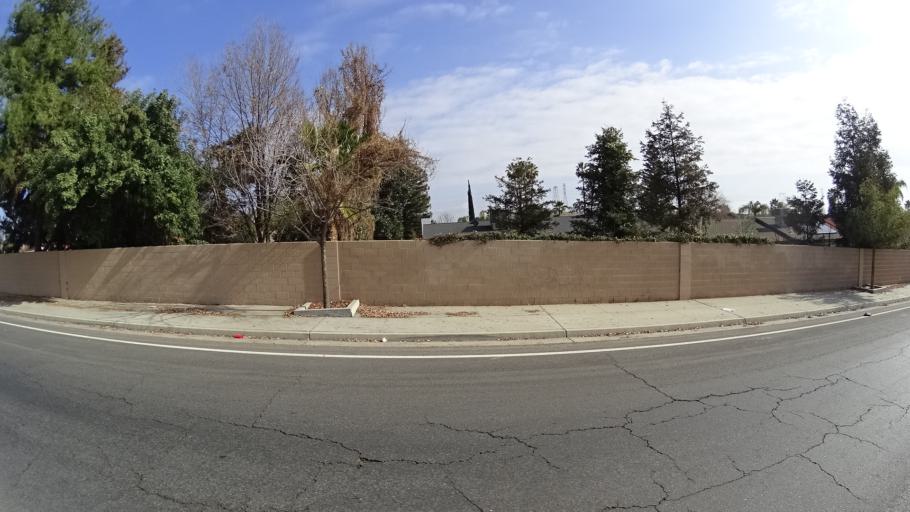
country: US
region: California
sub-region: Kern County
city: Bakersfield
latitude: 35.3917
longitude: -118.9285
